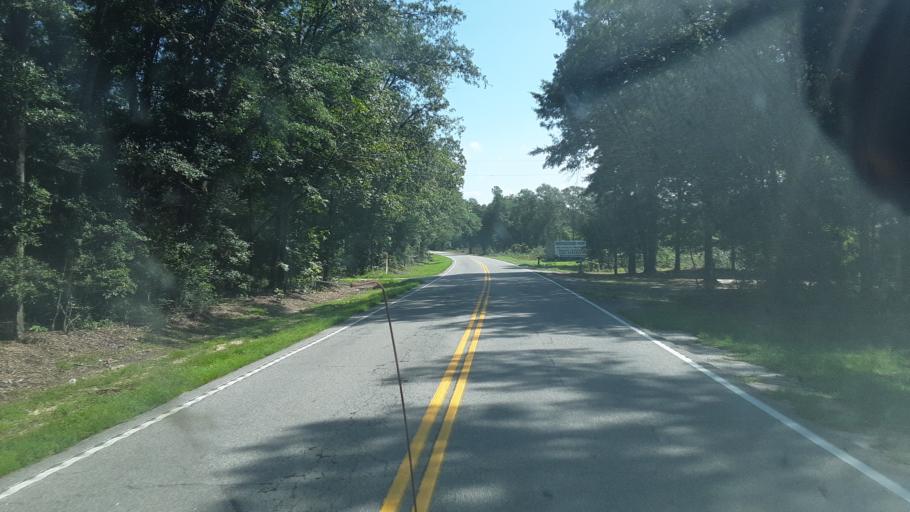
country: US
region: South Carolina
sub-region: Hampton County
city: Varnville
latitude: 32.8839
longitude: -81.0261
